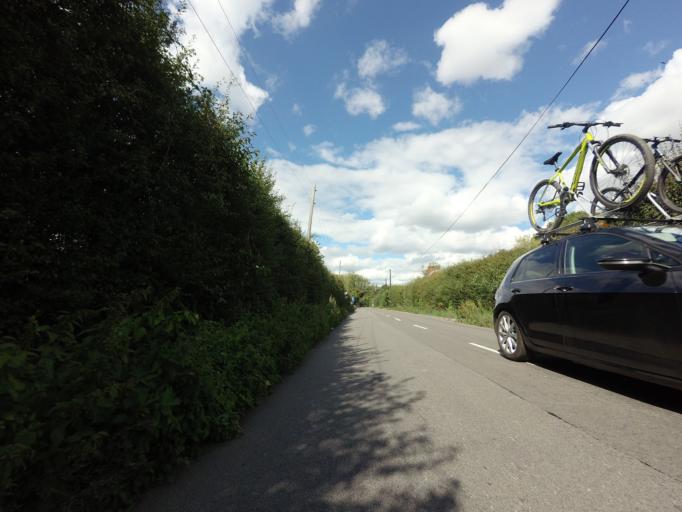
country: GB
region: England
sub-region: Kent
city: Marden
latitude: 51.1828
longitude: 0.4872
